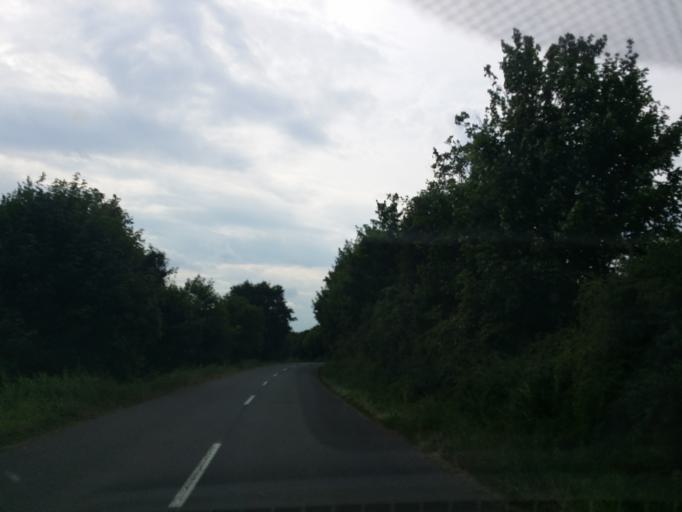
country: HU
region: Nograd
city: Bercel
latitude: 47.9771
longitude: 19.4111
